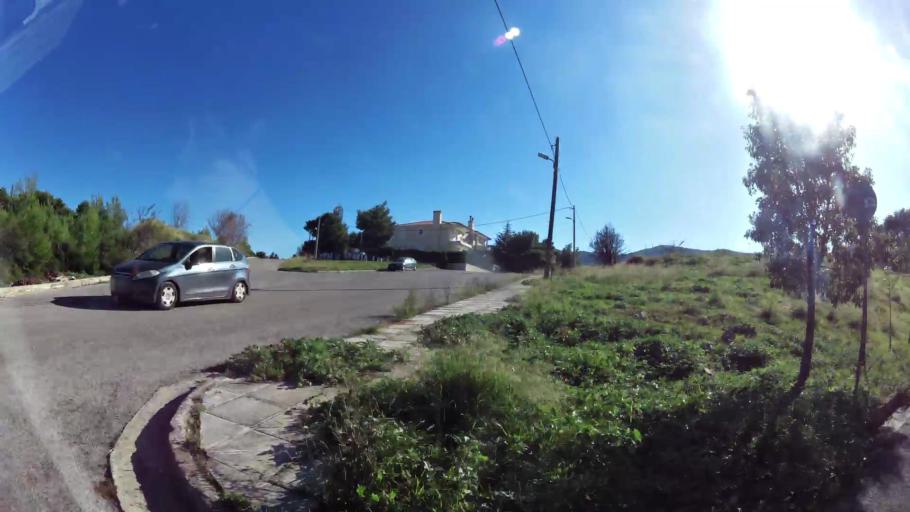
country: GR
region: Attica
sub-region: Nomarchia Anatolikis Attikis
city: Drosia
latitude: 38.1135
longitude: 23.8670
